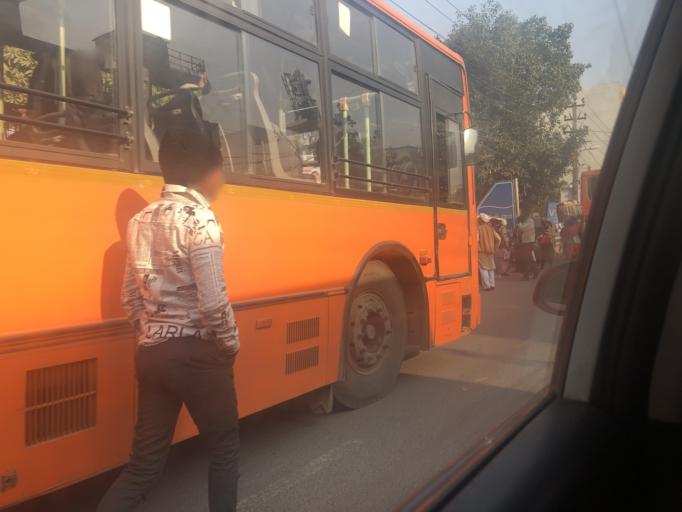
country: IN
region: Haryana
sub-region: Jhajjar
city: Bahadurgarh
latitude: 28.6148
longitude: 76.9777
